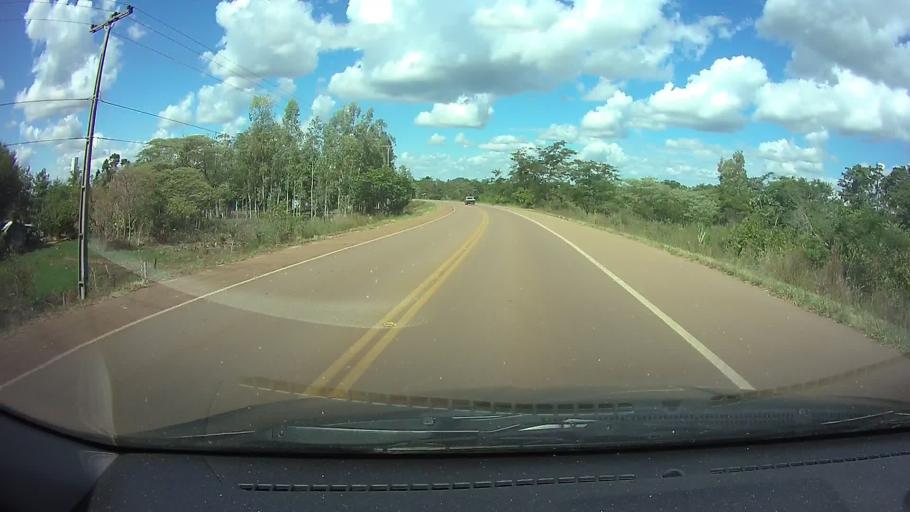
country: PY
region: Paraguari
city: La Colmena
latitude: -25.9188
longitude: -56.7230
